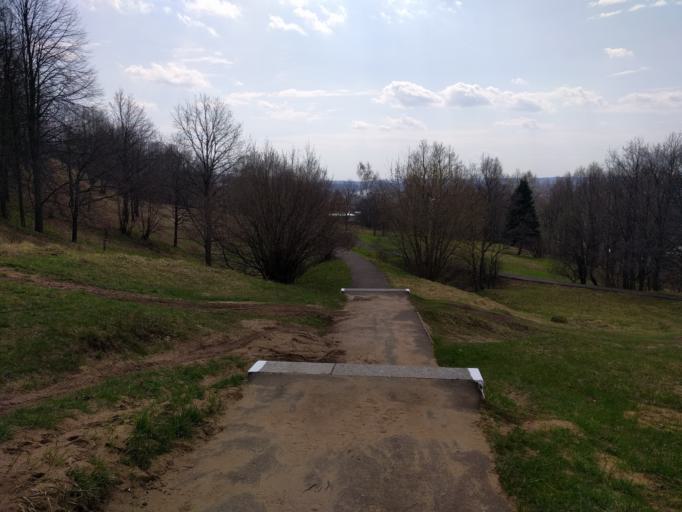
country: RU
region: Moskovskaya
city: Yakhroma
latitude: 56.2977
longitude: 37.5001
